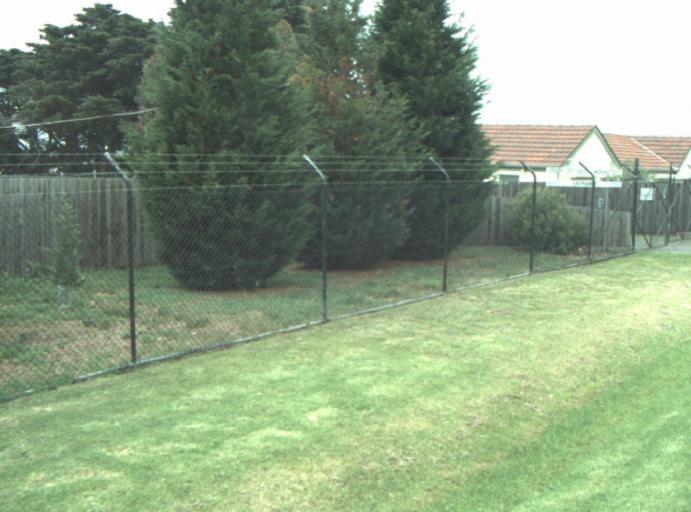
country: AU
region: Victoria
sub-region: Greater Geelong
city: Bell Post Hill
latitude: -38.0816
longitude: 144.3266
